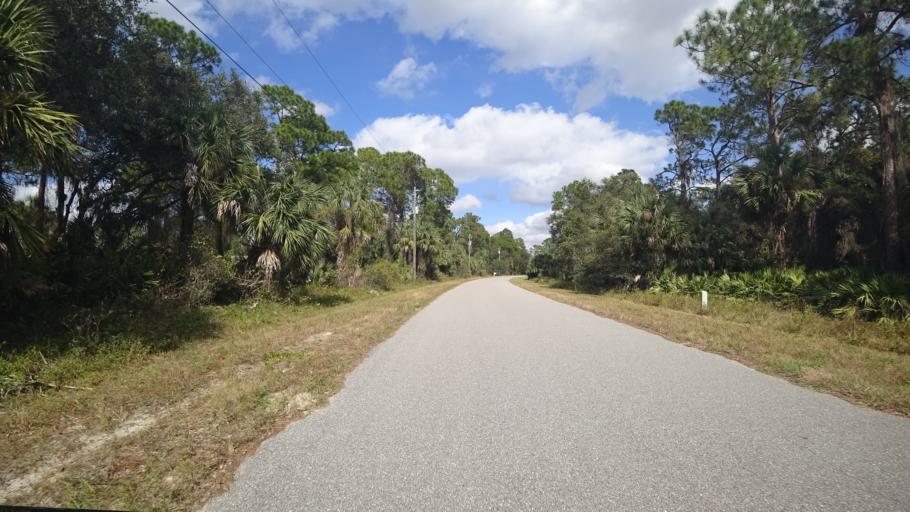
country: US
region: Florida
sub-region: Charlotte County
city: Port Charlotte
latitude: 27.0400
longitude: -82.1347
